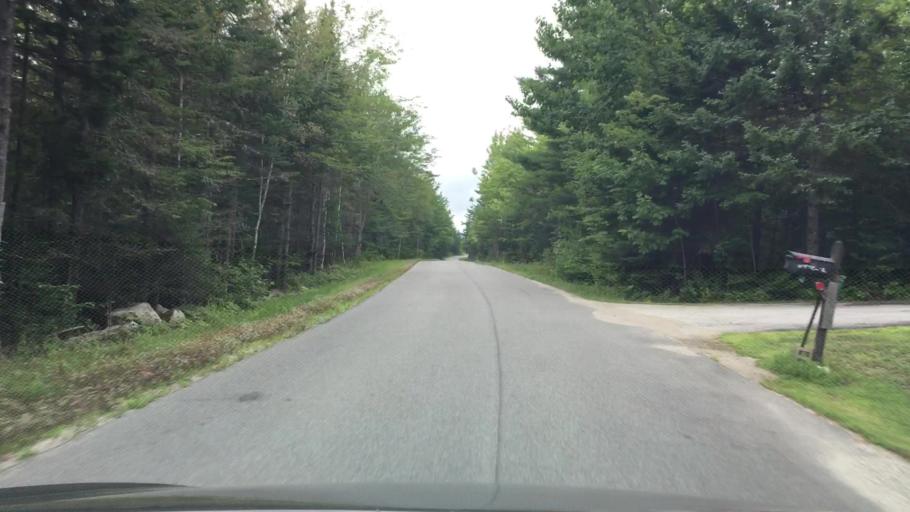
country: US
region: Maine
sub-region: Waldo County
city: Stockton Springs
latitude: 44.5186
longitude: -68.8772
